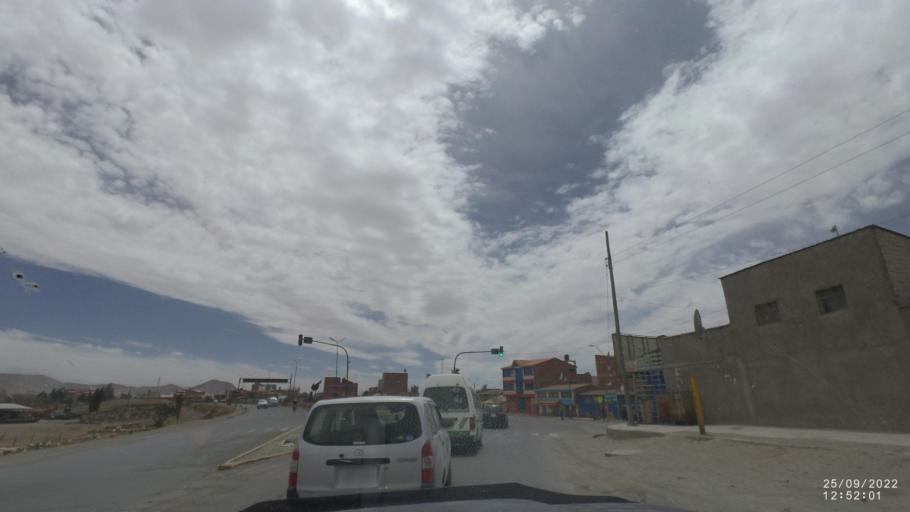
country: BO
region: Oruro
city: Oruro
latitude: -17.9805
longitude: -67.0509
